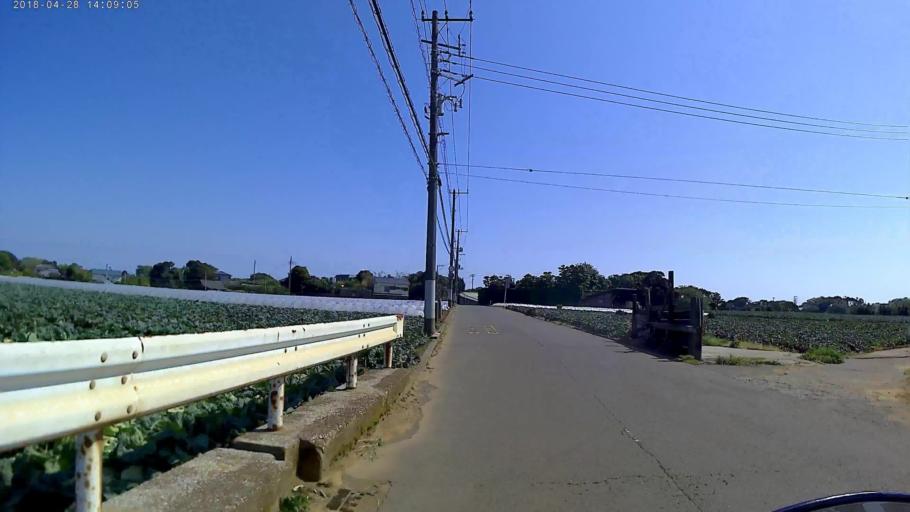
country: JP
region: Kanagawa
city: Miura
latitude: 35.1482
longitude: 139.6514
